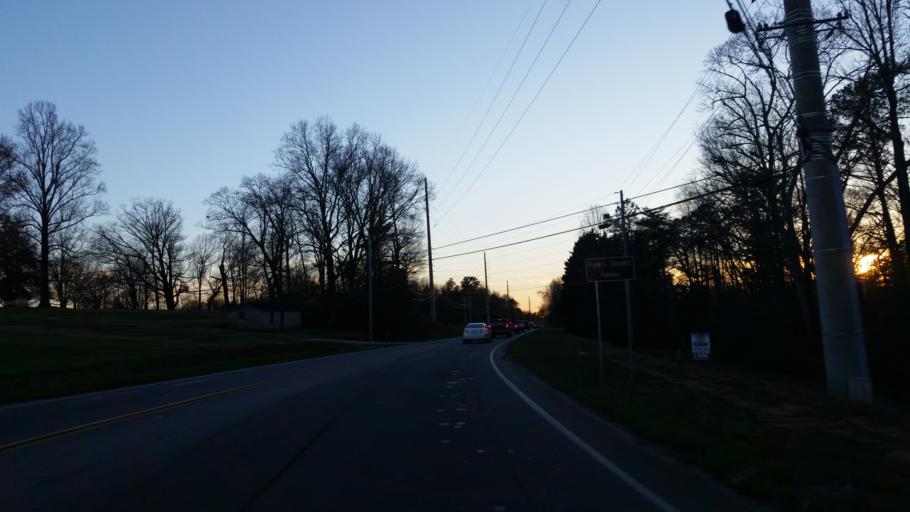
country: US
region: Georgia
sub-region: Hall County
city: Oakwood
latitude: 34.3017
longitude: -83.9803
